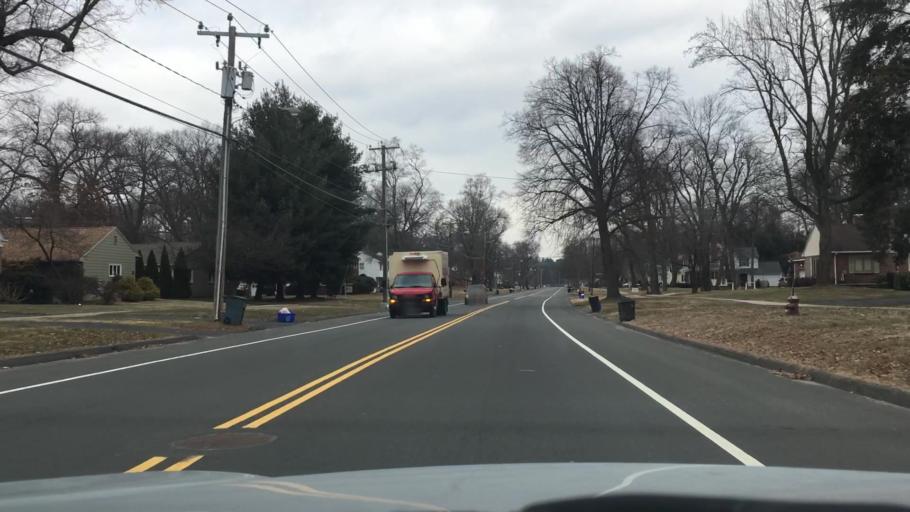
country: US
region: Massachusetts
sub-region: Hampden County
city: Longmeadow
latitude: 42.0506
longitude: -72.5733
